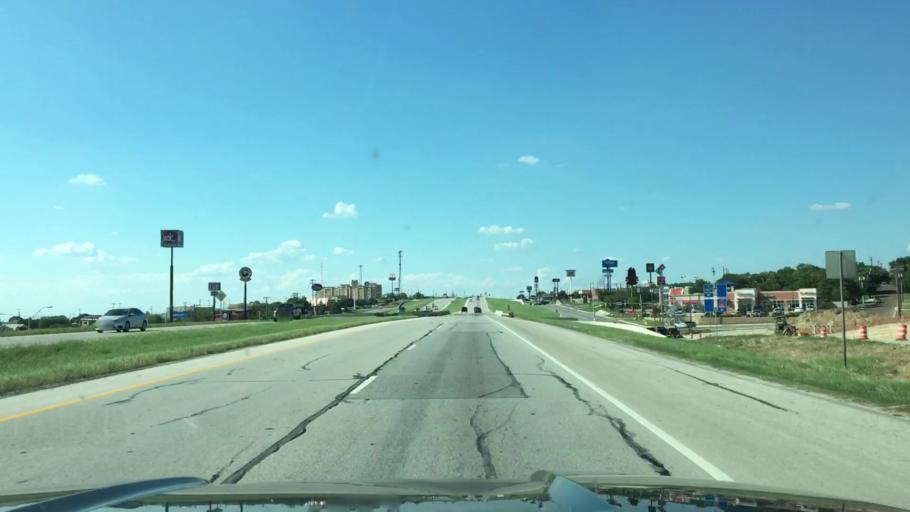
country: US
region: Texas
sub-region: Wise County
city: Decatur
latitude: 33.2264
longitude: -97.5924
